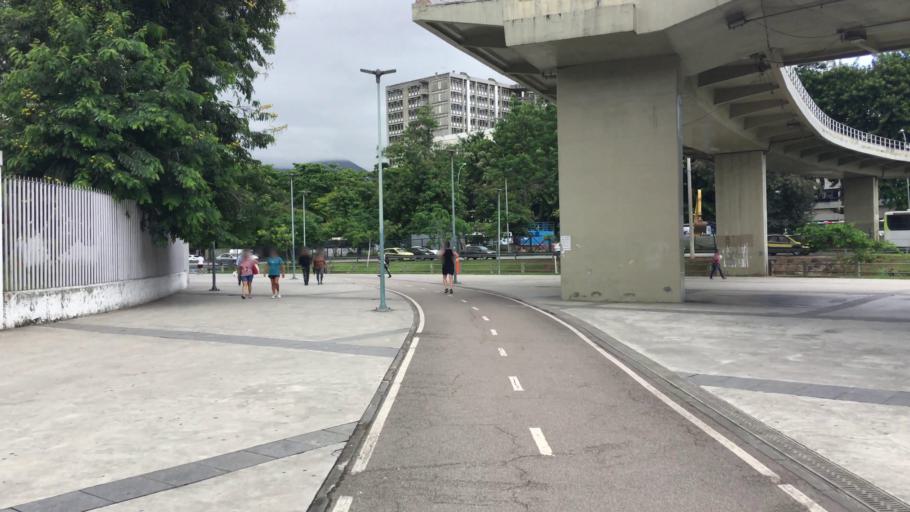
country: BR
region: Rio de Janeiro
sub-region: Rio De Janeiro
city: Rio de Janeiro
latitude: -22.9111
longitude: -43.2329
